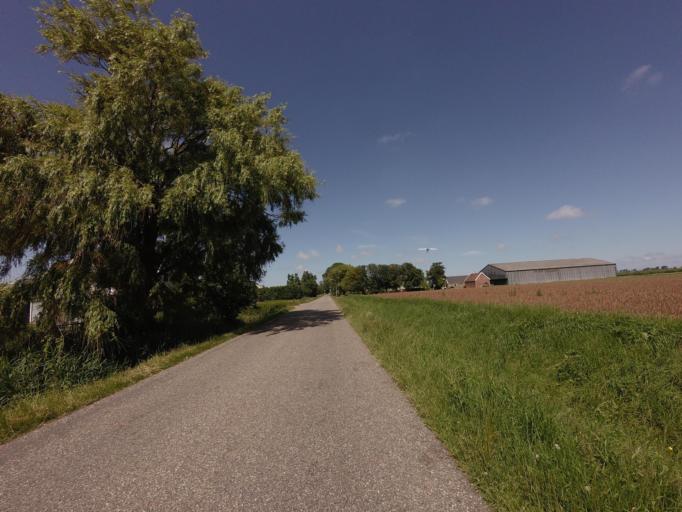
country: NL
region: North Holland
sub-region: Gemeente Schagen
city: Schagen
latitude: 52.8814
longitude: 4.8396
